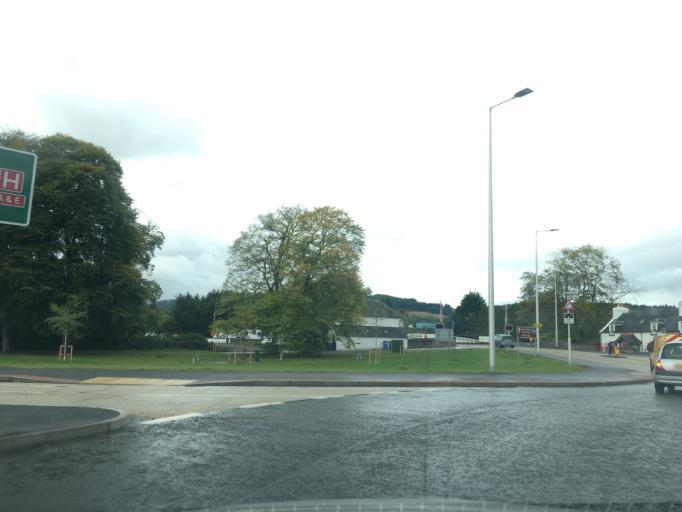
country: GB
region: Scotland
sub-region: Highland
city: Inverness
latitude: 57.4649
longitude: -4.2422
